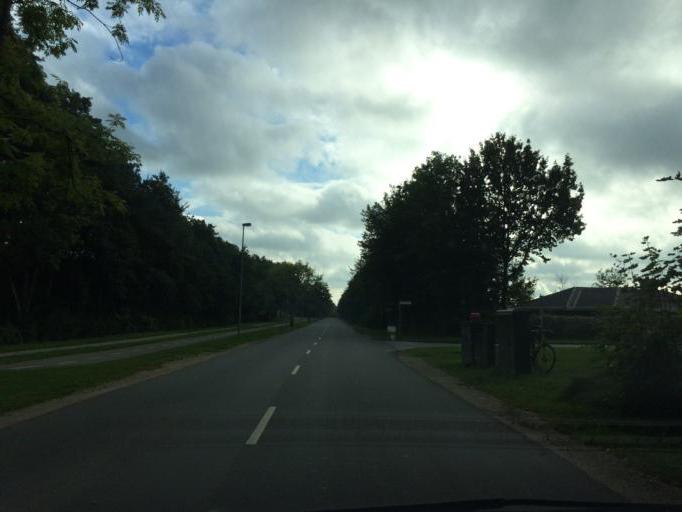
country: DK
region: North Denmark
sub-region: Bronderslev Kommune
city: Dronninglund
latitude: 57.1547
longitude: 10.2748
